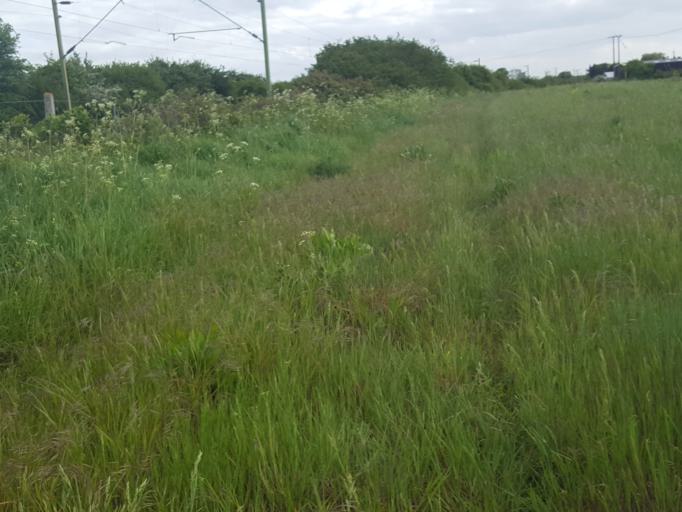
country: GB
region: England
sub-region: Essex
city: Clacton-on-Sea
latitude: 51.8189
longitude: 1.1809
